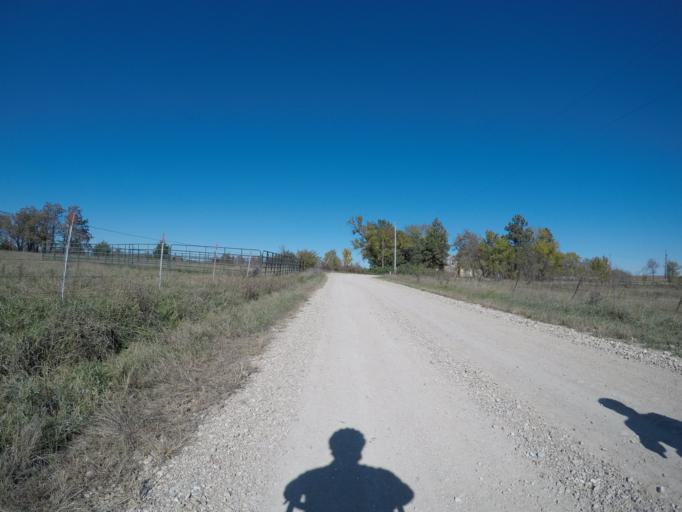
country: US
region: Kansas
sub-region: Wabaunsee County
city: Alma
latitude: 39.0575
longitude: -96.3582
